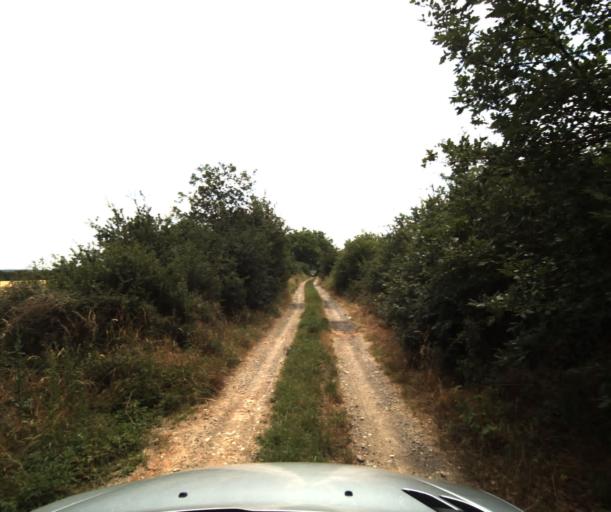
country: FR
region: Midi-Pyrenees
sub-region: Departement de la Haute-Garonne
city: Lacasse
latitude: 43.4121
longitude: 1.2682
